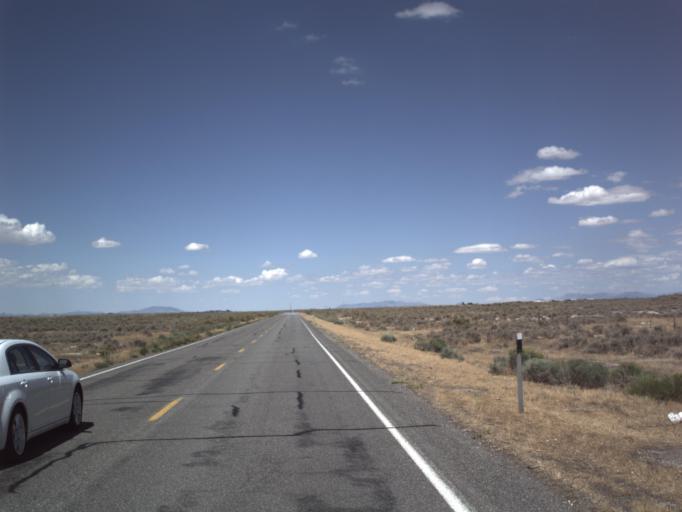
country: US
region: Utah
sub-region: Millard County
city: Delta
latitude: 39.2995
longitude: -112.4712
